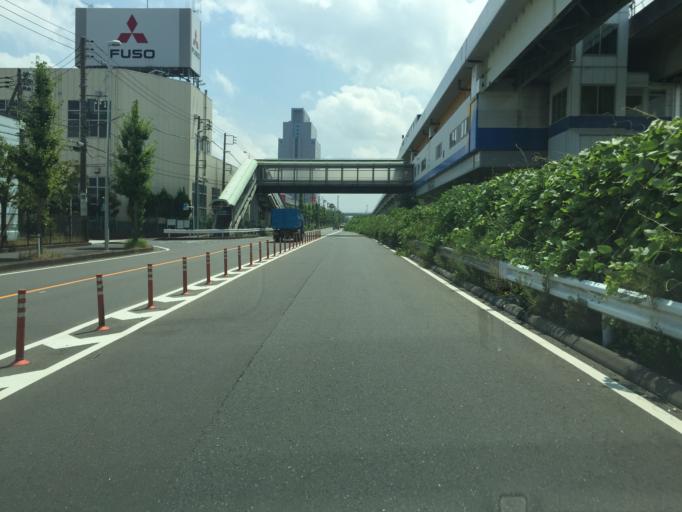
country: JP
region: Kanagawa
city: Yokosuka
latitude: 35.3589
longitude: 139.6438
